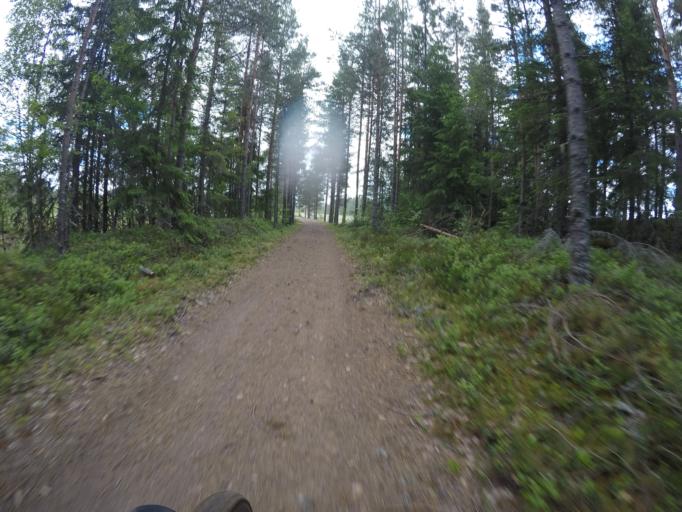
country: SE
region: Vaermland
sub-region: Filipstads Kommun
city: Lesjofors
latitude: 60.1408
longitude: 14.2517
